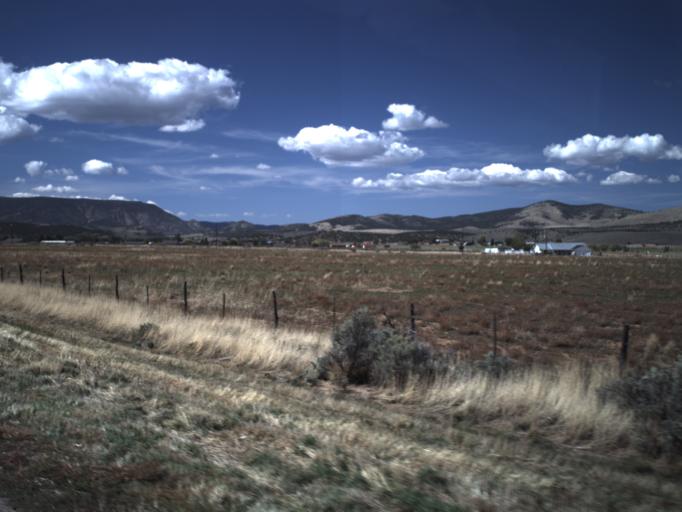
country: US
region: Utah
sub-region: Washington County
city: Enterprise
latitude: 37.5780
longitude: -113.6943
